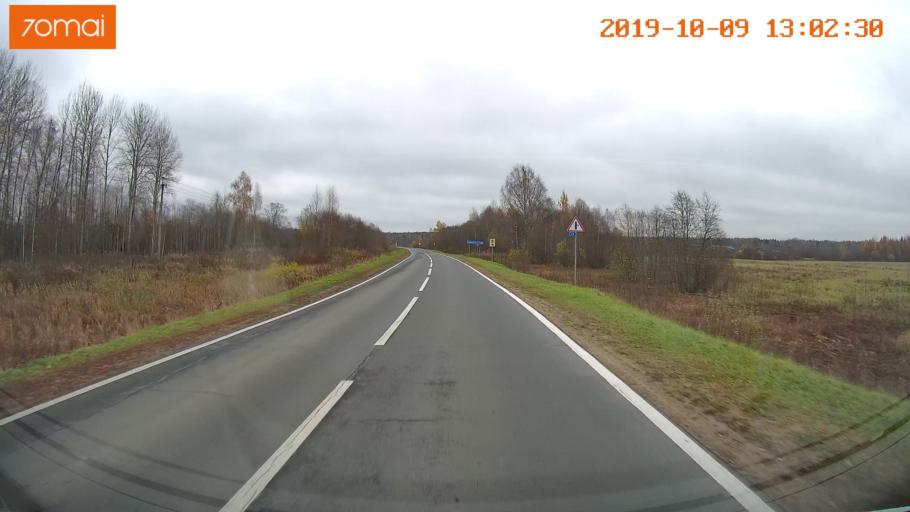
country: RU
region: Jaroslavl
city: Prechistoye
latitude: 58.3610
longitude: 40.5029
